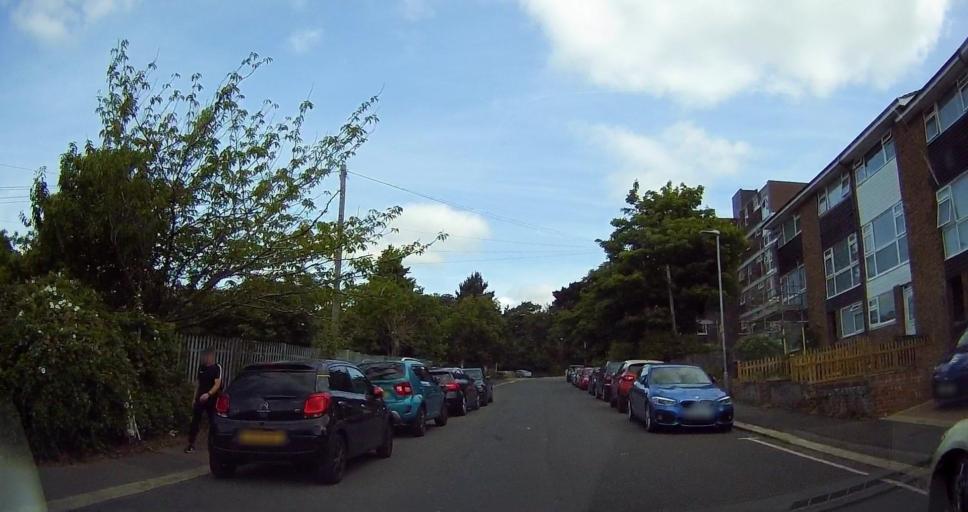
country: GB
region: England
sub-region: East Sussex
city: Hastings
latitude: 50.8587
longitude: 0.5631
